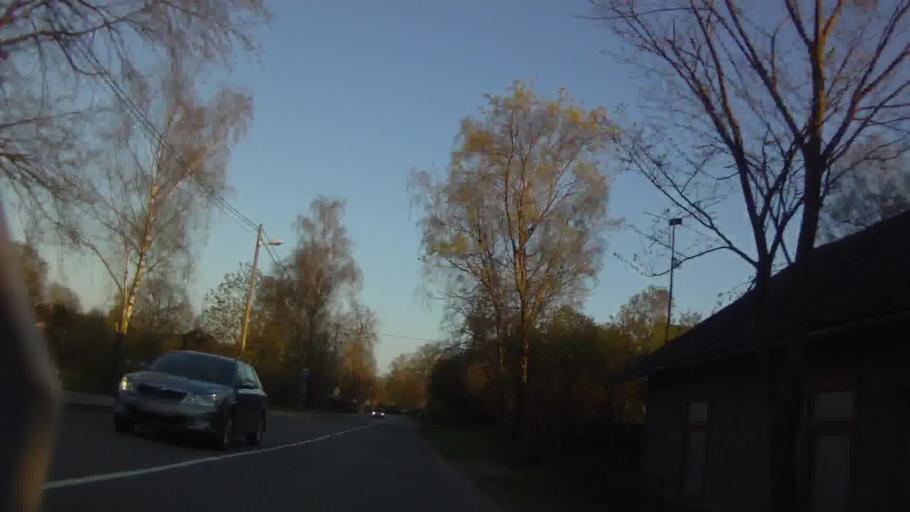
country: LV
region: Riga
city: Jaunciems
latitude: 57.0399
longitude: 24.1748
